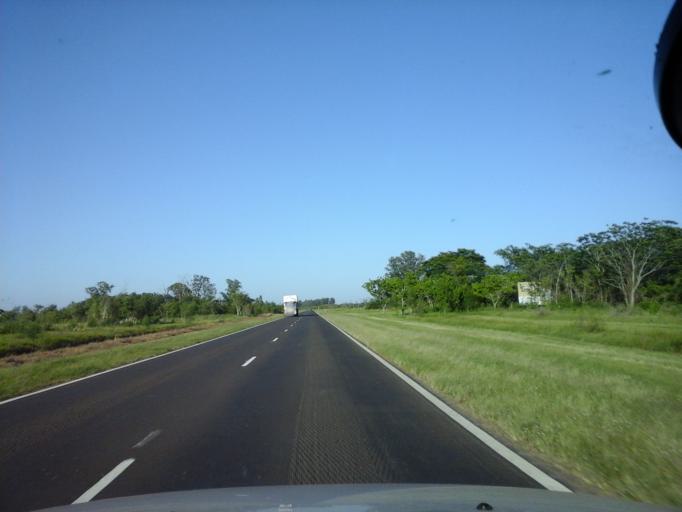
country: AR
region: Corrientes
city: Ita Ibate
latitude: -27.4444
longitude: -57.3813
